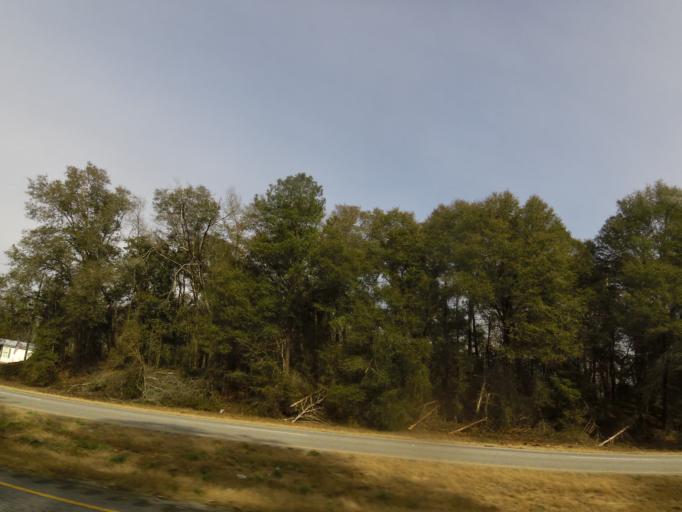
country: US
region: Alabama
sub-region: Dale County
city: Midland City
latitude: 31.3223
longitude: -85.5203
